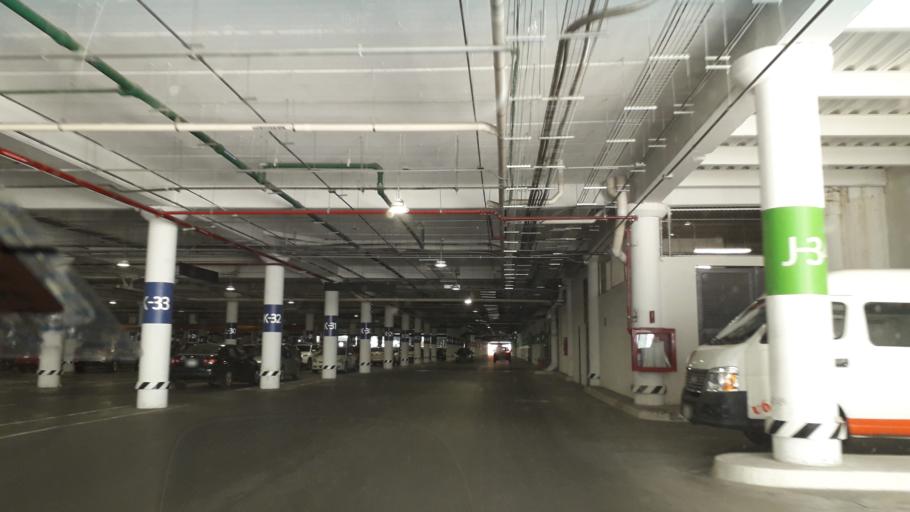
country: MX
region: Puebla
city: Puebla
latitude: 19.0337
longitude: -98.2283
